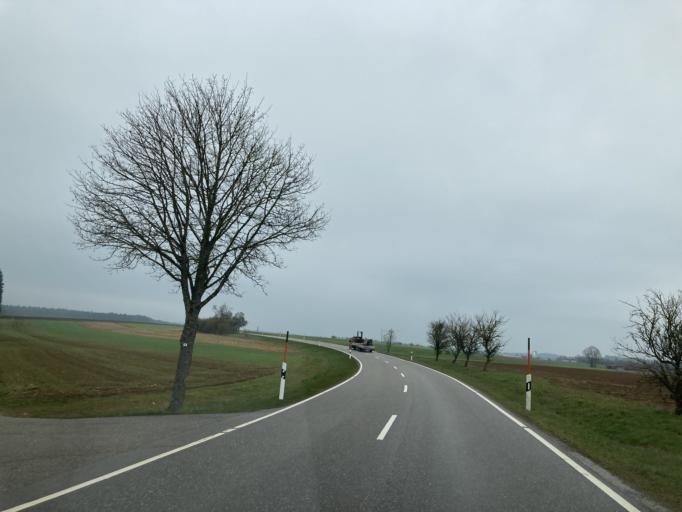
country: DE
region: Baden-Wuerttemberg
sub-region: Freiburg Region
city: Dornhan
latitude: 48.3443
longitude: 8.4736
